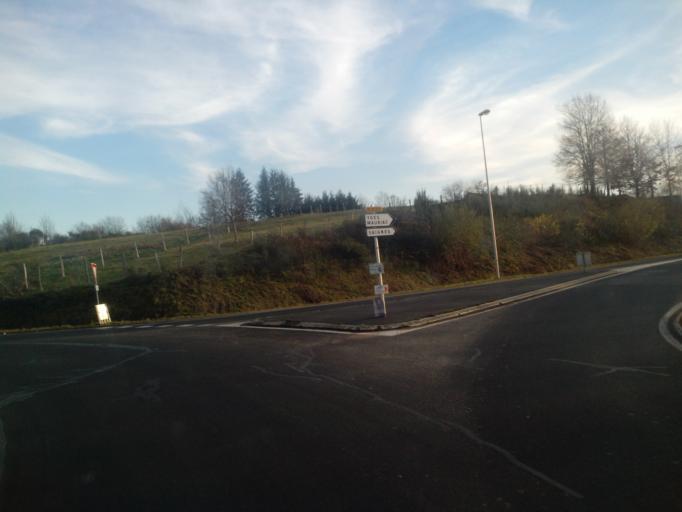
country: FR
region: Auvergne
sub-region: Departement du Cantal
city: Ydes
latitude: 45.3611
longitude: 2.4703
